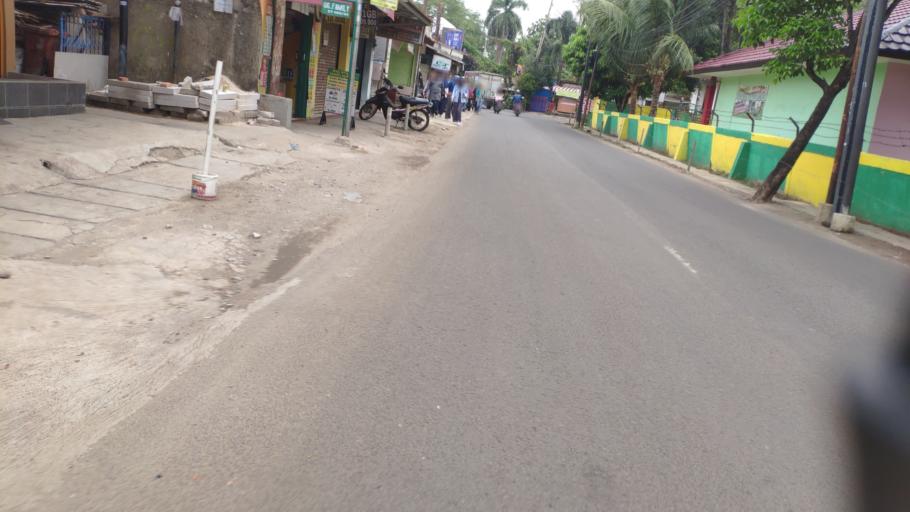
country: ID
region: West Java
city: Depok
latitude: -6.3459
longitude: 106.8264
